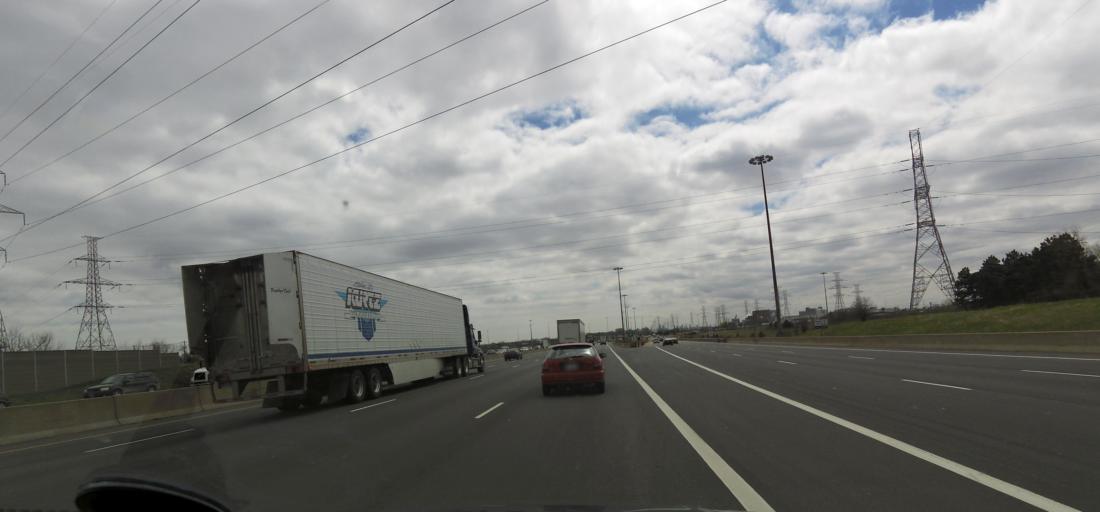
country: CA
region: Ontario
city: Etobicoke
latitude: 43.6822
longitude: -79.5752
